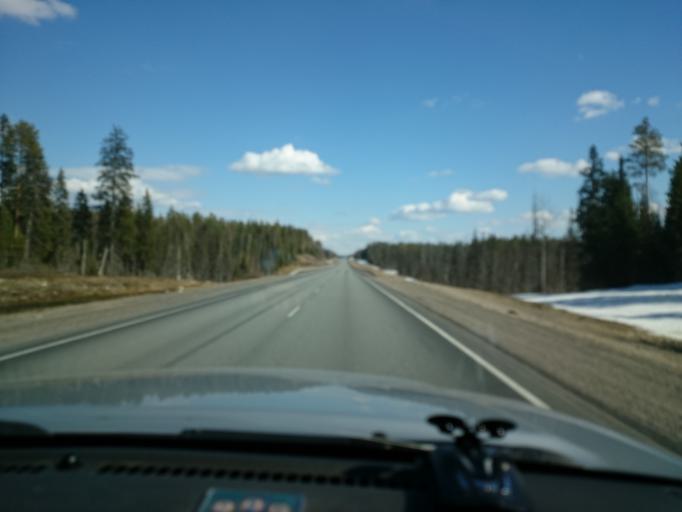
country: RU
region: Republic of Karelia
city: Pryazha
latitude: 61.5201
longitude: 33.4687
